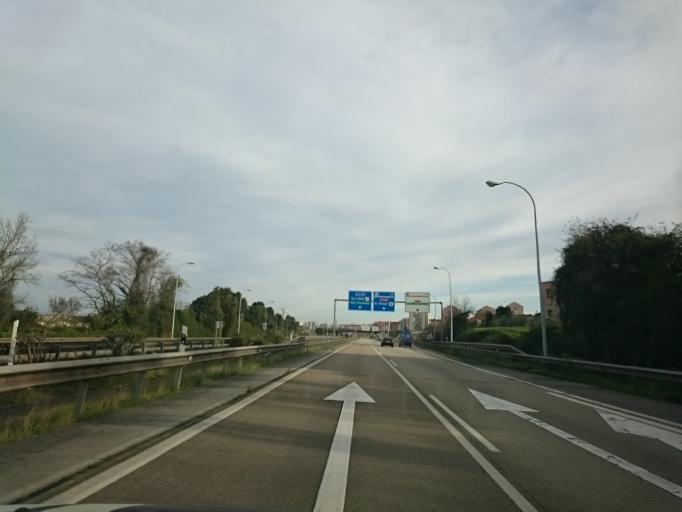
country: ES
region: Asturias
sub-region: Province of Asturias
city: Natahoyo
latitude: 43.5222
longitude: -5.6945
